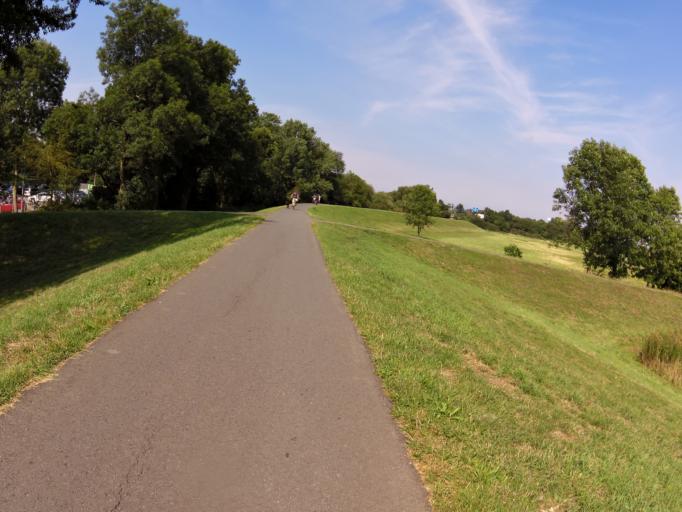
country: DE
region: Bremen
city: Bremen
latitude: 53.0279
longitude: 8.8635
